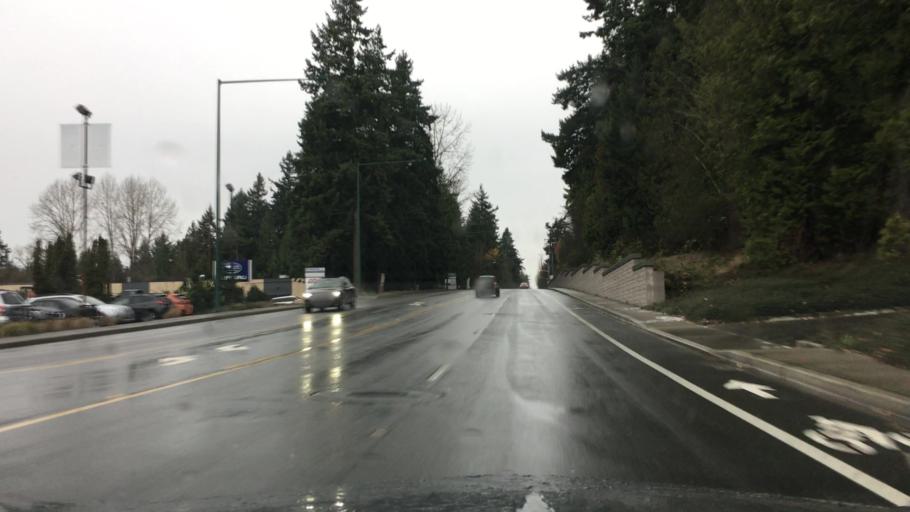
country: US
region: Washington
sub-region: King County
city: Kingsgate
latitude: 47.7041
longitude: -122.1833
